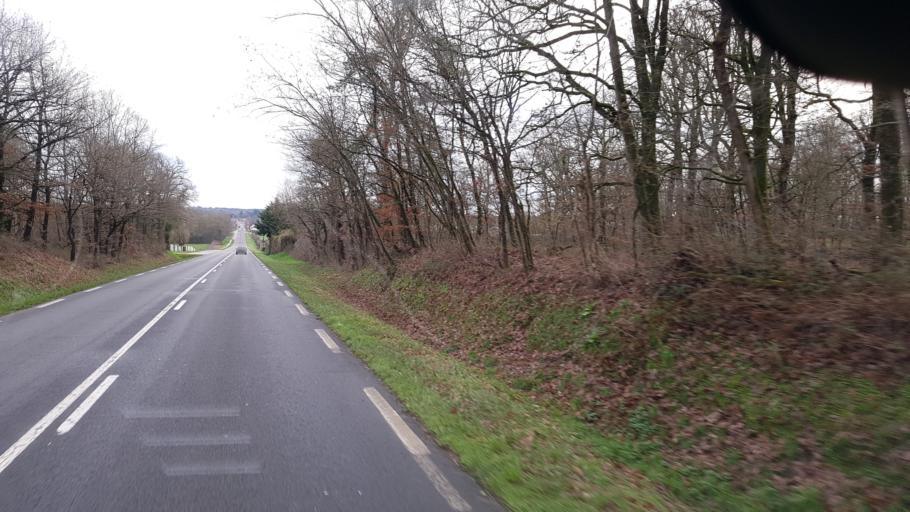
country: FR
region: Centre
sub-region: Departement du Loir-et-Cher
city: Lamotte-Beuvron
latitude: 47.6184
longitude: 2.0149
